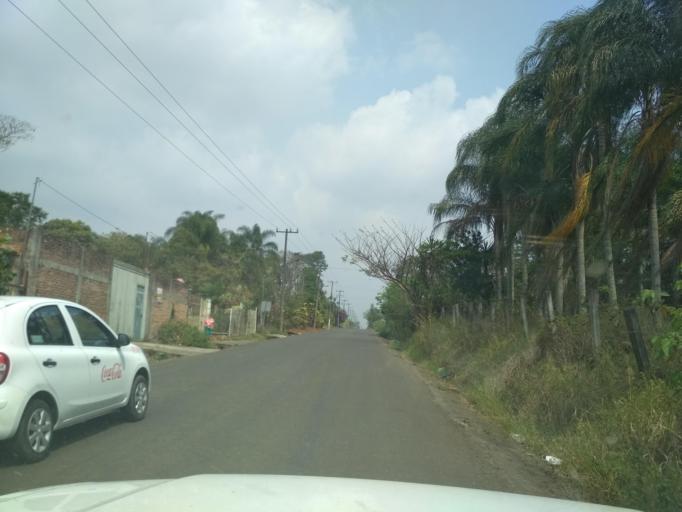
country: MX
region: Veracruz
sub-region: Cordoba
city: Fredepo
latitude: 18.8614
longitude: -96.9838
